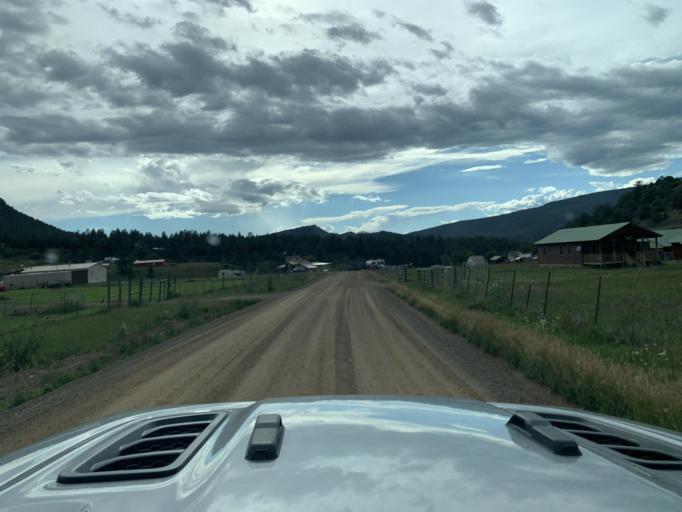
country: US
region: Colorado
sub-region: Archuleta County
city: Pagosa Springs
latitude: 37.2208
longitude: -107.1866
